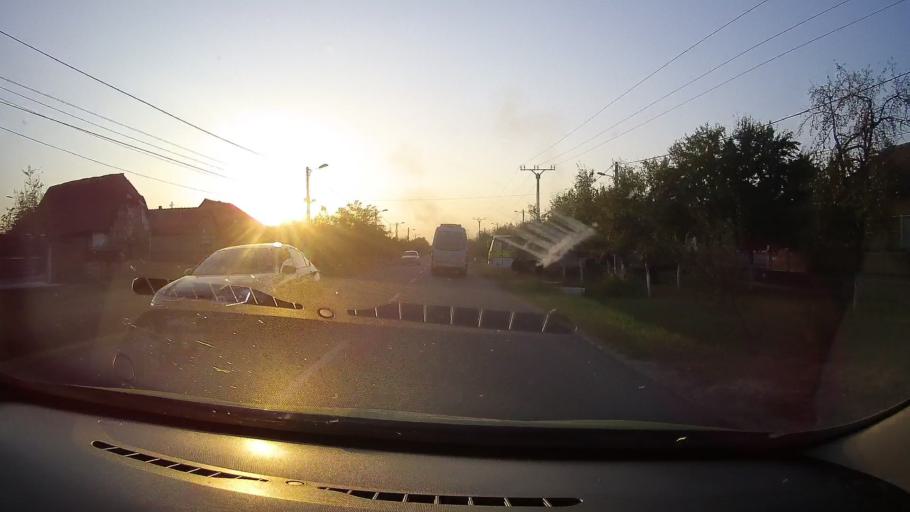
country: RO
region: Arad
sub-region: Comuna Sicula
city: Sicula
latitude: 46.4366
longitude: 21.7659
